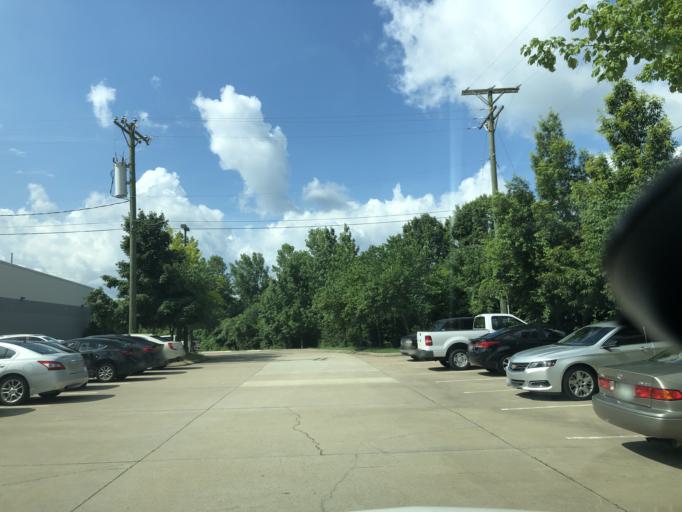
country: US
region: Tennessee
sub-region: Rutherford County
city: La Vergne
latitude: 36.0285
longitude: -86.6102
